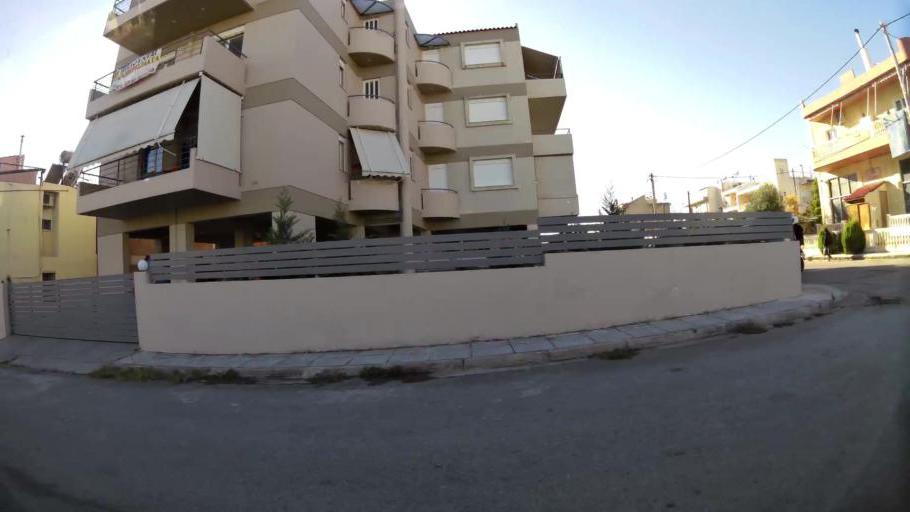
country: GR
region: Attica
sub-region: Nomarchia Anatolikis Attikis
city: Acharnes
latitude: 38.0917
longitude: 23.7245
